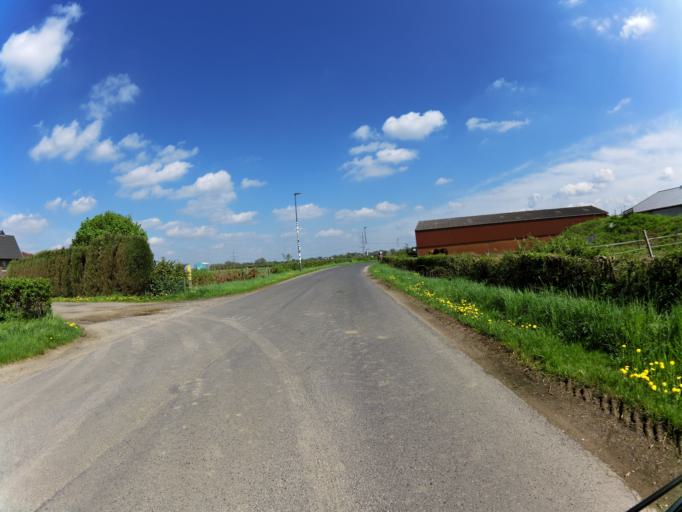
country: NL
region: Limburg
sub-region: Gemeente Kerkrade
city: Kerkrade
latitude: 50.8282
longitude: 6.0561
